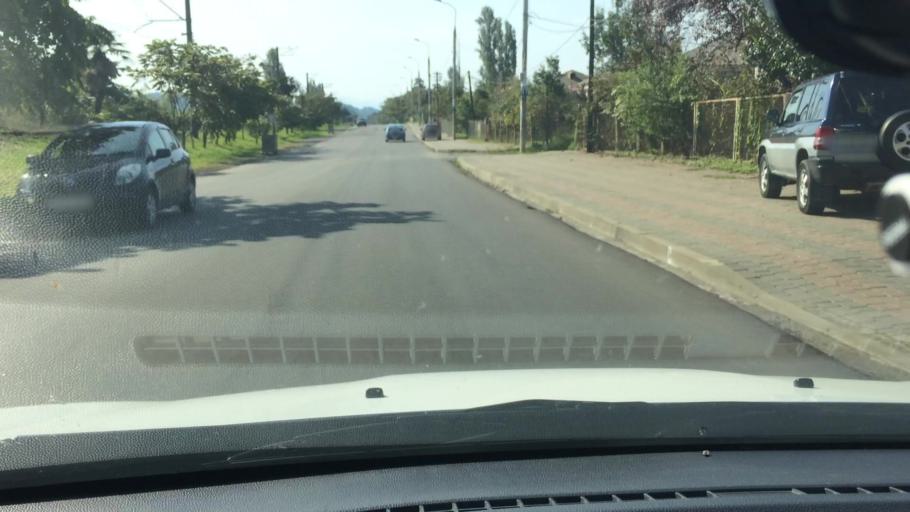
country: GE
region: Ajaria
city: Kobuleti
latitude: 41.8006
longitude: 41.7744
